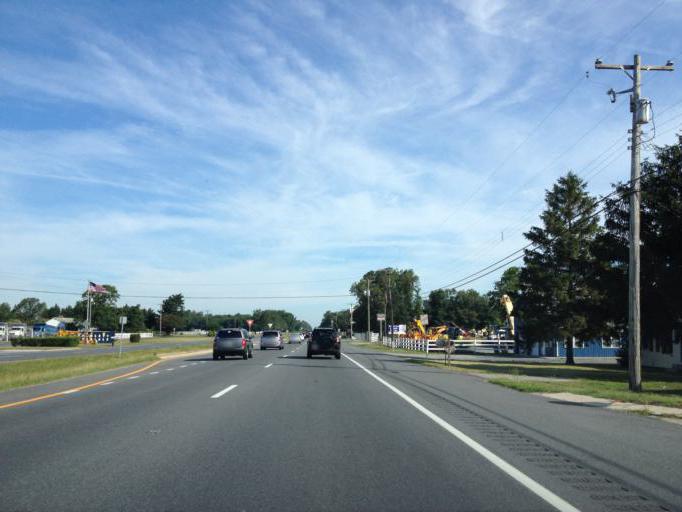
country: US
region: Delaware
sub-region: Sussex County
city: Georgetown
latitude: 38.6344
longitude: -75.3503
